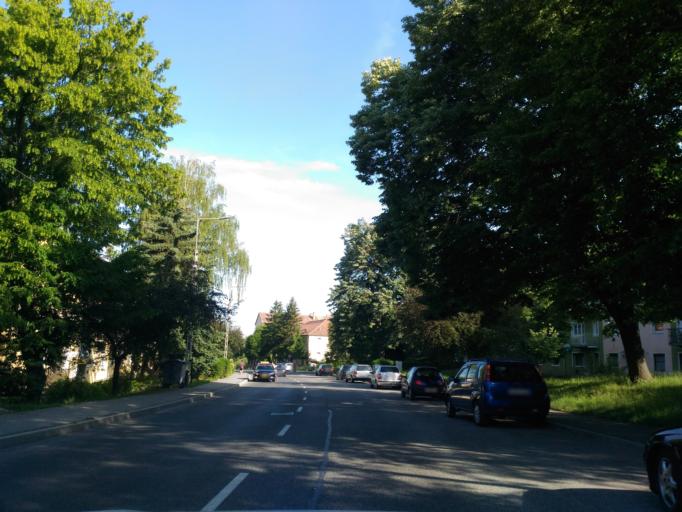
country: HU
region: Baranya
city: Komlo
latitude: 46.1835
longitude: 18.2590
